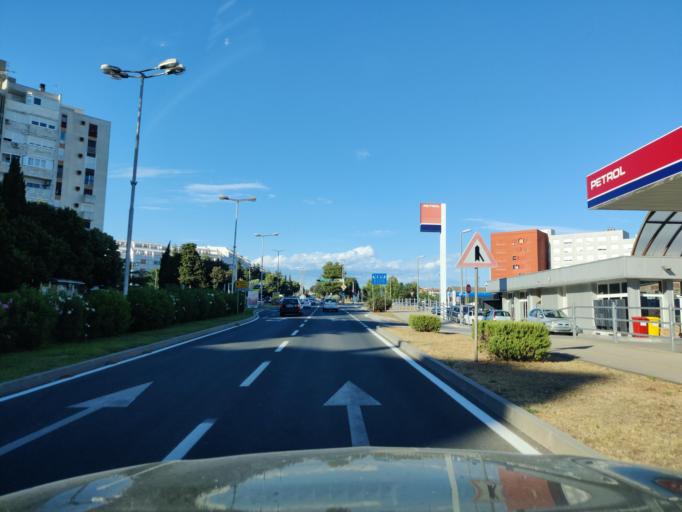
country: HR
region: Zadarska
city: Zadar
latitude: 44.1104
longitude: 15.2480
